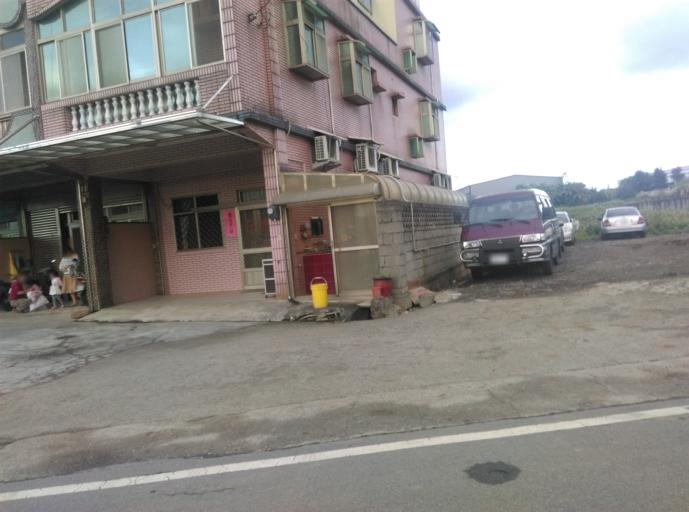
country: TW
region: Taiwan
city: Taoyuan City
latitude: 24.9952
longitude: 121.2512
